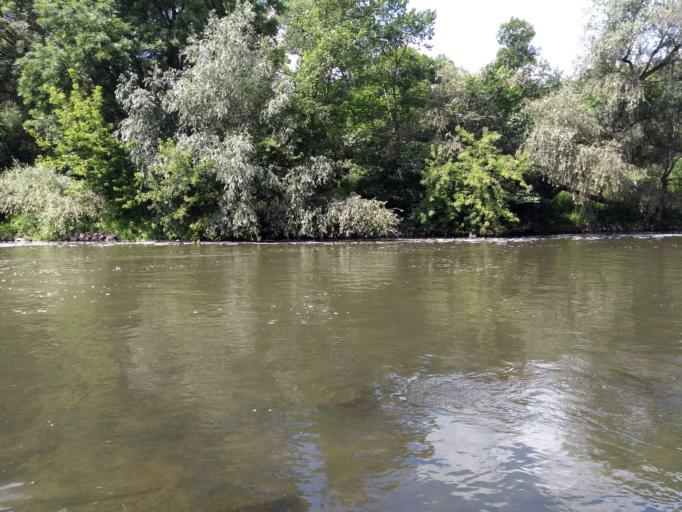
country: DE
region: Saxony-Anhalt
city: Halle Neustadt
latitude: 51.4572
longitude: 11.9405
